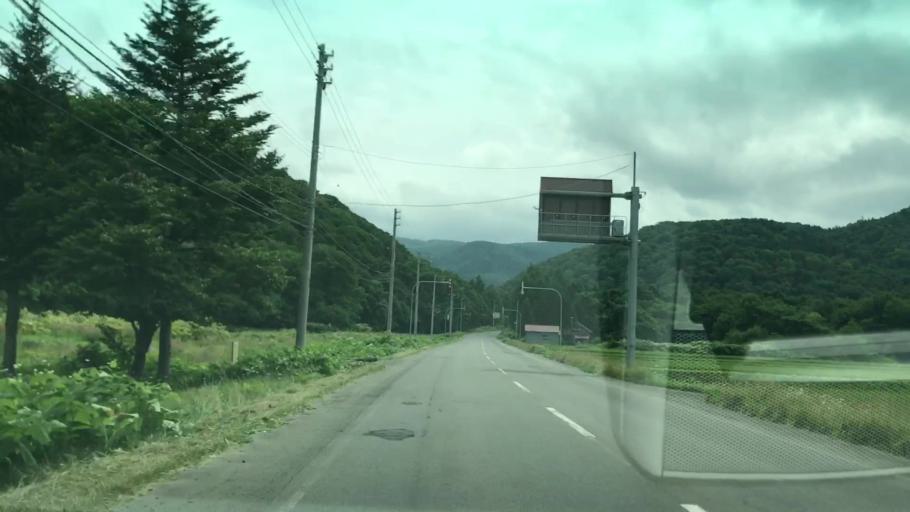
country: JP
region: Hokkaido
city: Yoichi
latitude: 43.0484
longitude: 140.8473
